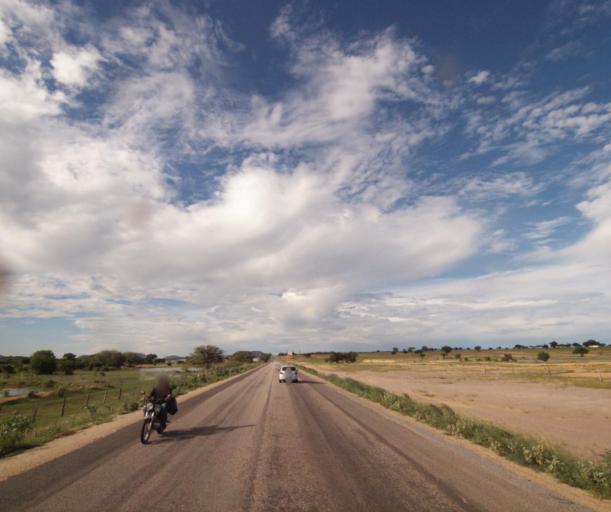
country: BR
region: Bahia
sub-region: Guanambi
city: Guanambi
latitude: -14.2752
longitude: -42.7833
